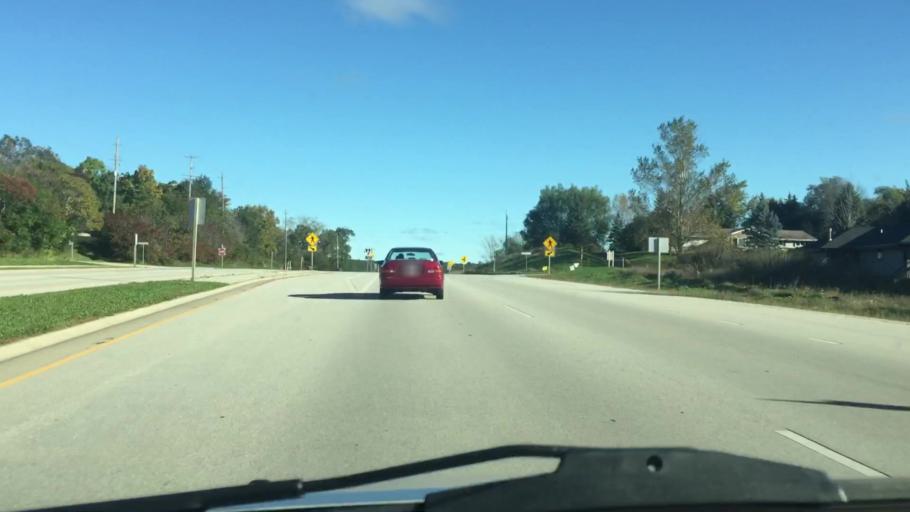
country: US
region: Wisconsin
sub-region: Waukesha County
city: Wales
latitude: 43.0147
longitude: -88.3837
